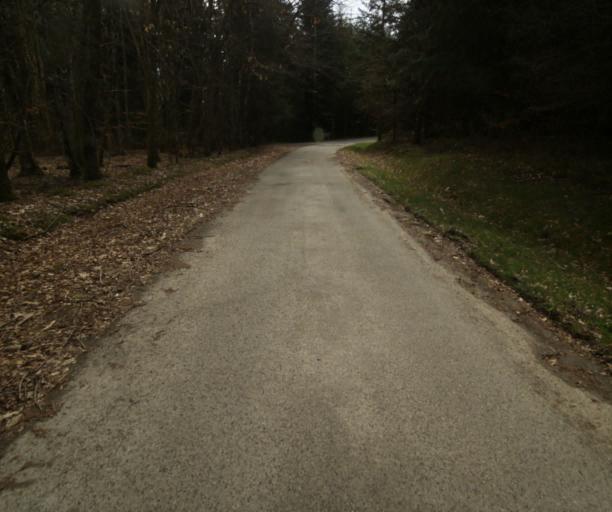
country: FR
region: Limousin
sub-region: Departement de la Correze
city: Correze
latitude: 45.2981
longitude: 1.9580
